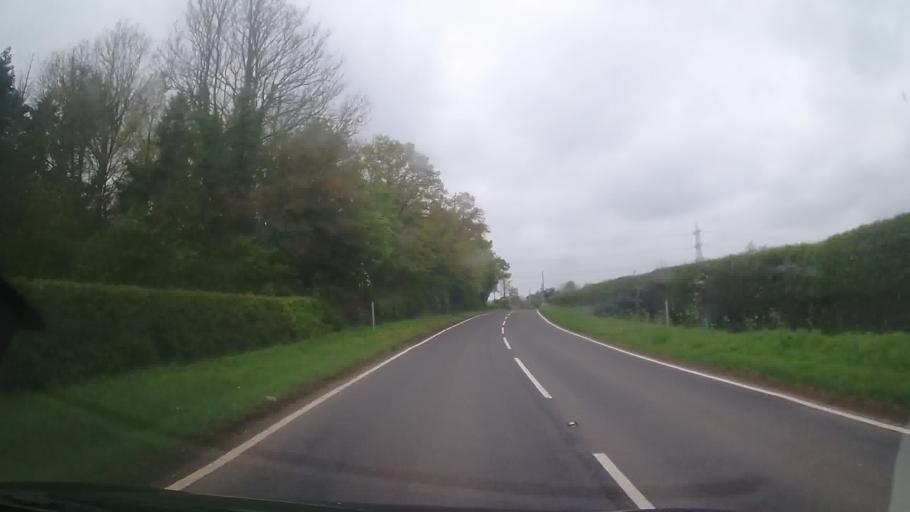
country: GB
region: Wales
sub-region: Wrexham
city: Ruabon
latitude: 52.9812
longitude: -3.0133
